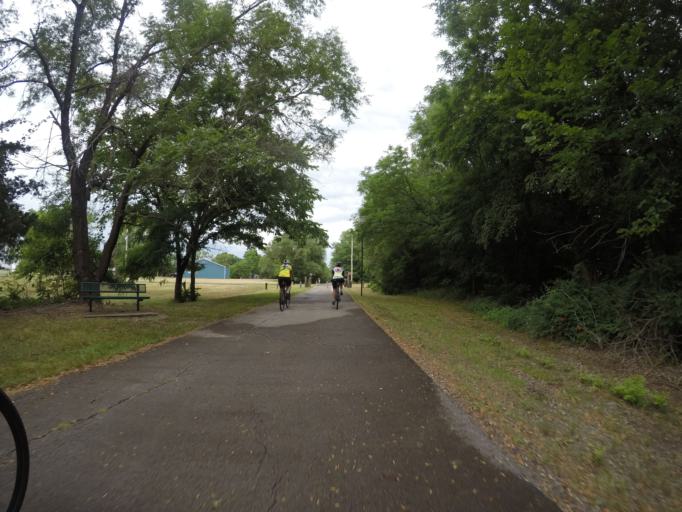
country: US
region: Kansas
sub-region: Anderson County
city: Garnett
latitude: 38.2731
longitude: -95.2422
